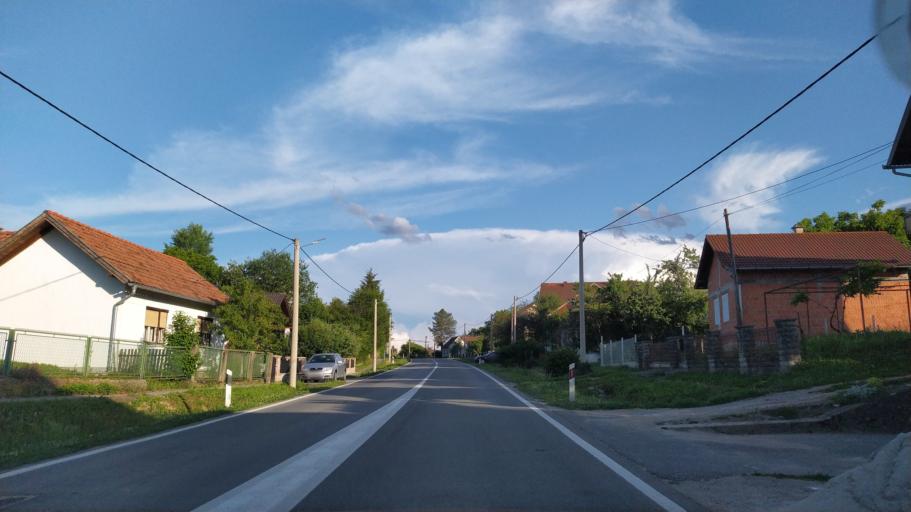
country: HR
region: Virovitick-Podravska
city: Cacinci
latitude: 45.6108
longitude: 17.8112
